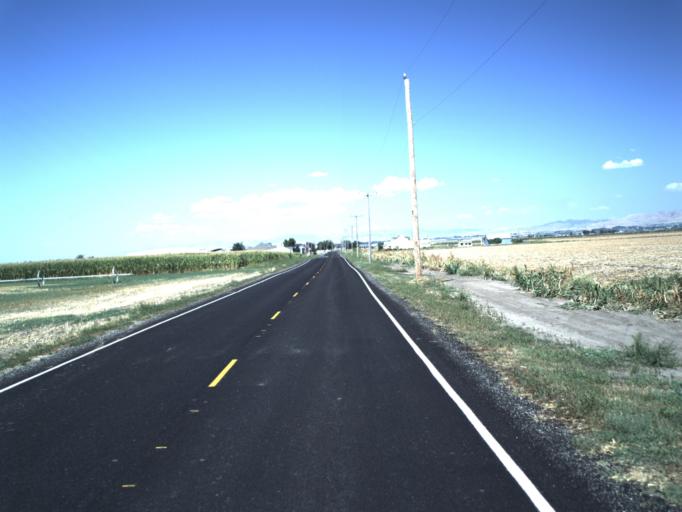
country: US
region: Utah
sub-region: Cache County
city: Lewiston
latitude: 41.9833
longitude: -111.8763
